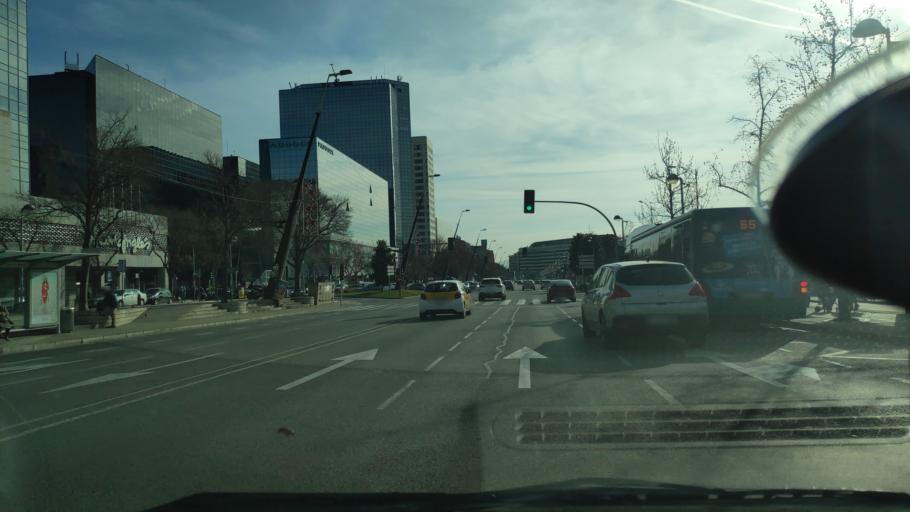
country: ES
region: Catalonia
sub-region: Provincia de Barcelona
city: Sabadell
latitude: 41.5547
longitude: 2.0975
